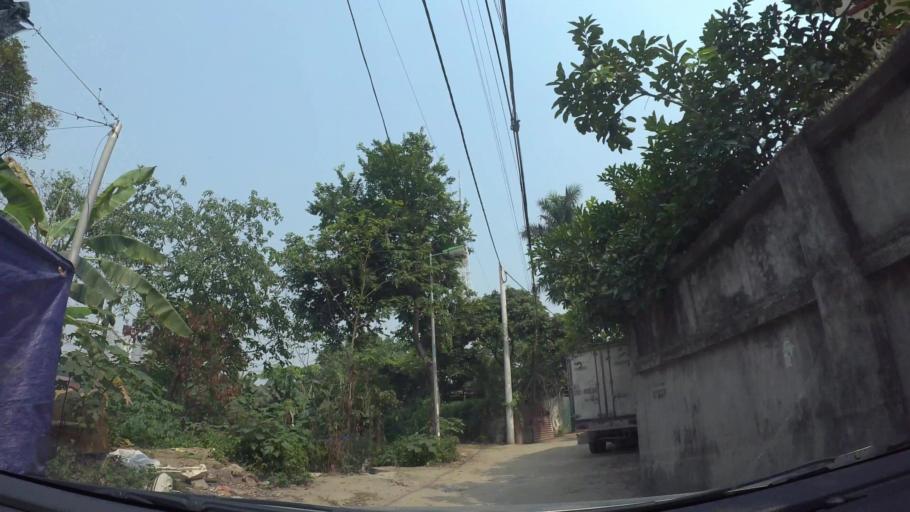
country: VN
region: Ha Noi
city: Cau Dien
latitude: 21.0039
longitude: 105.7606
